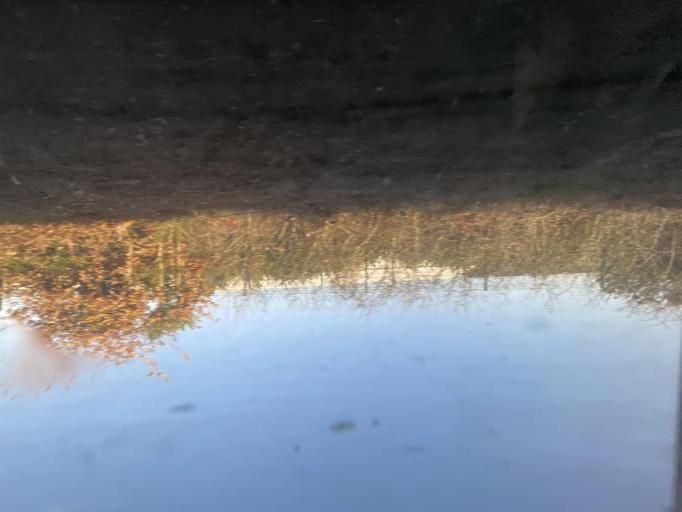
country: FR
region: Pays de la Loire
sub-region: Departement de la Loire-Atlantique
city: Sainte-Luce-sur-Loire
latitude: 47.2510
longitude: -1.4639
